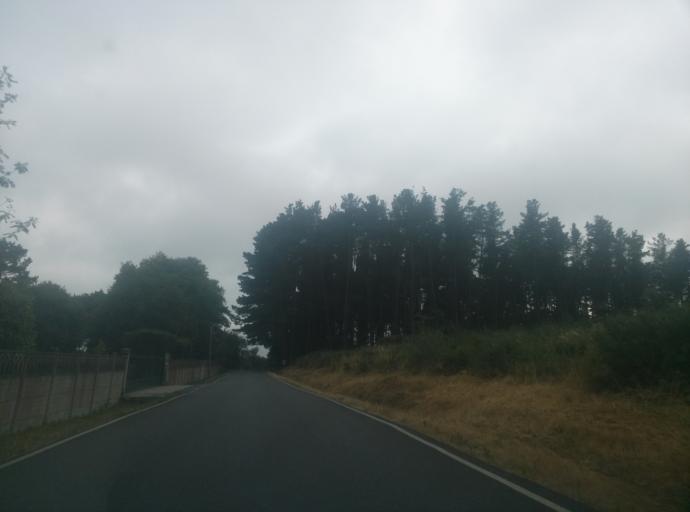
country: ES
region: Galicia
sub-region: Provincia de Lugo
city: Lugo
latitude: 43.0725
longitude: -7.5549
